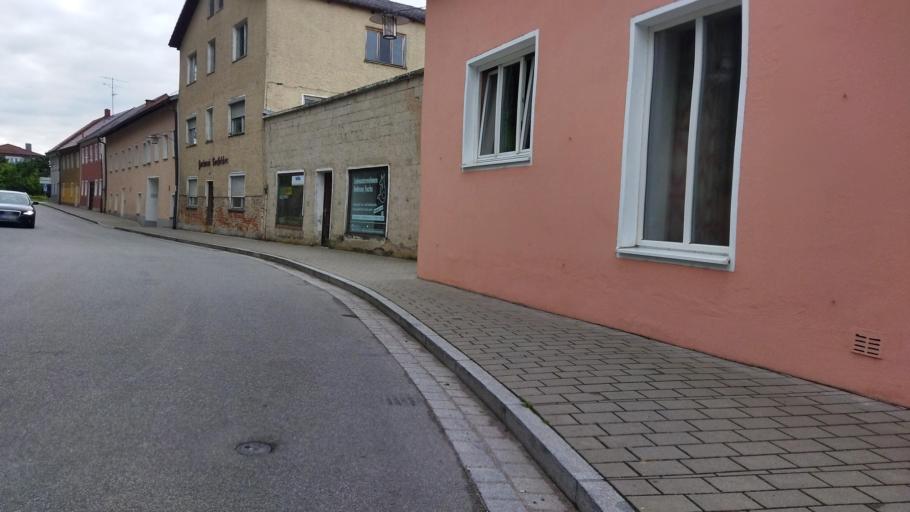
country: DE
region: Bavaria
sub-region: Upper Palatinate
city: Worth an der Donau
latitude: 48.9995
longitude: 12.4009
